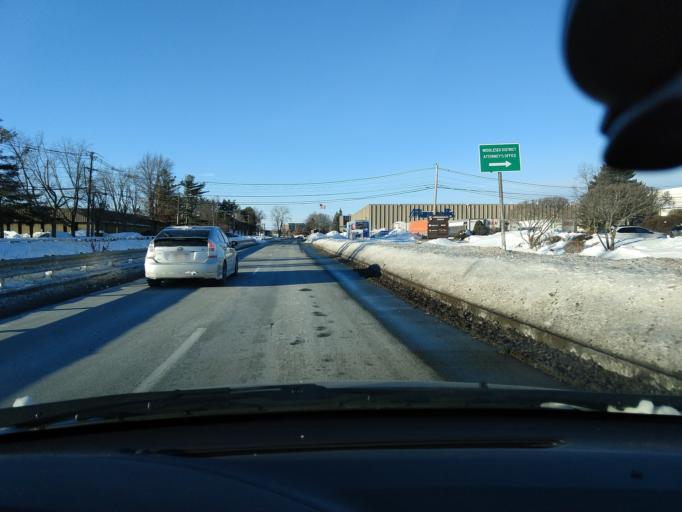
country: US
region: Massachusetts
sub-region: Middlesex County
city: Woburn
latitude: 42.5119
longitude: -71.1338
